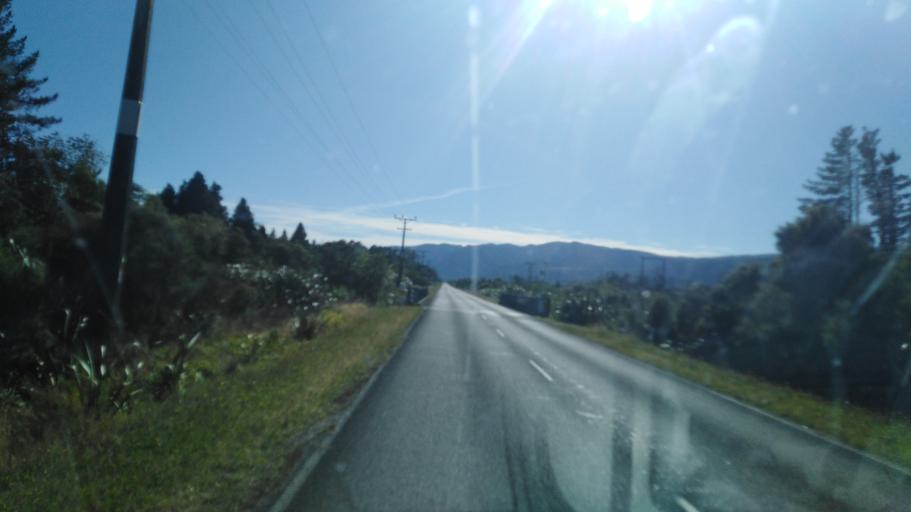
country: NZ
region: West Coast
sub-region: Buller District
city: Westport
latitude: -41.7453
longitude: 171.6858
